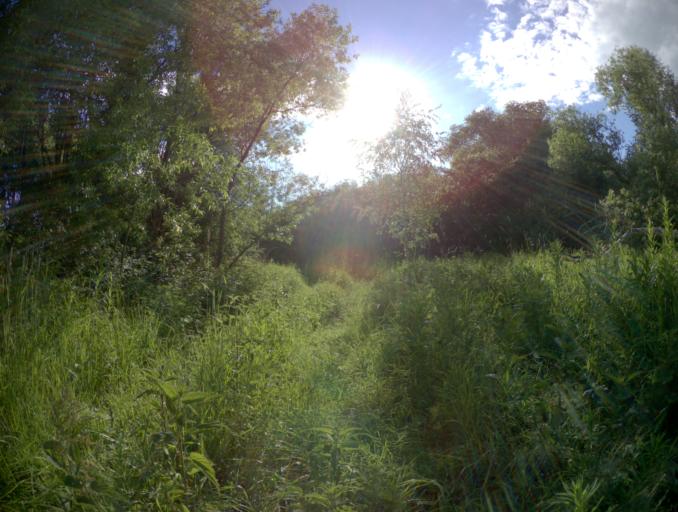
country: RU
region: Vladimir
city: Stavrovo
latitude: 56.2539
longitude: 40.1655
